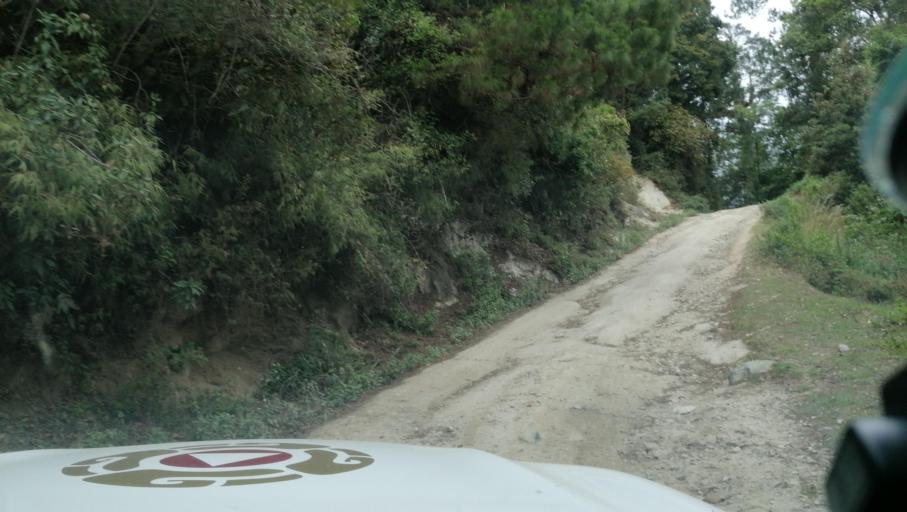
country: MX
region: Chiapas
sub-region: Cacahoatan
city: Benito Juarez
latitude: 15.1963
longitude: -92.2306
